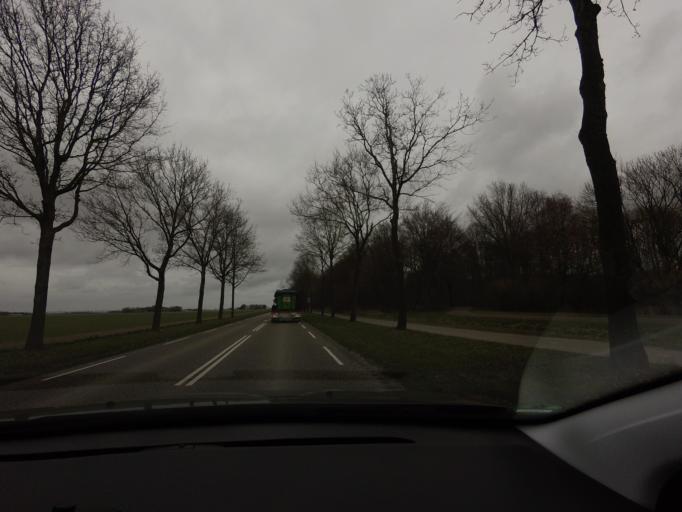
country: NL
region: Flevoland
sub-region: Gemeente Noordoostpolder
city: Emmeloord
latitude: 52.7131
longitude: 5.7197
